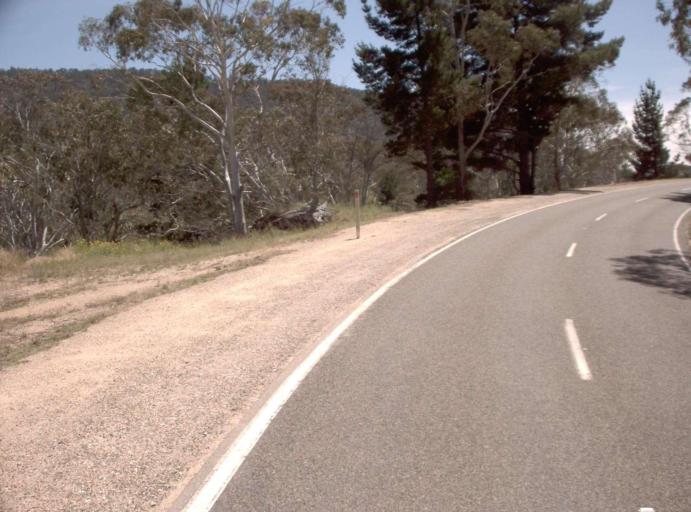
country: AU
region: Victoria
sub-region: Alpine
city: Mount Beauty
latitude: -37.1095
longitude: 147.5774
